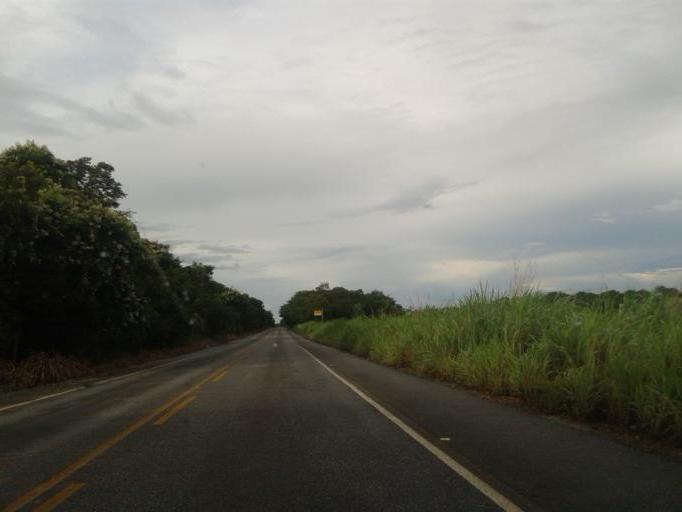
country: BR
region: Goias
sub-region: Mozarlandia
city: Mozarlandia
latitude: -14.8708
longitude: -50.5511
